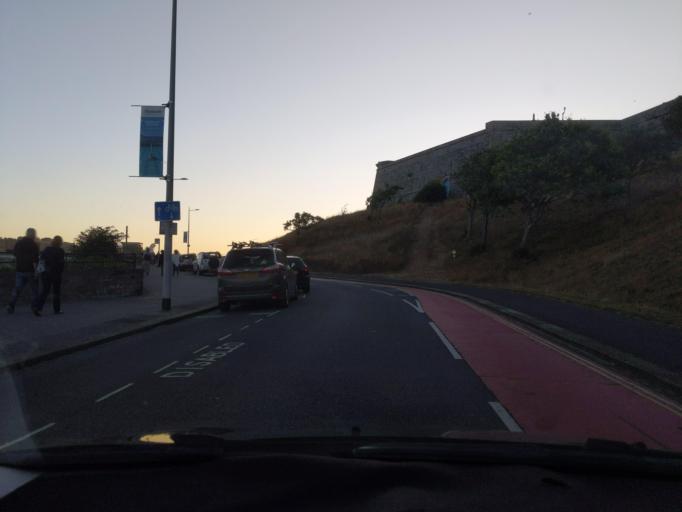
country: GB
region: England
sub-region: Plymouth
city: Plymouth
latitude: 50.3632
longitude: -4.1342
